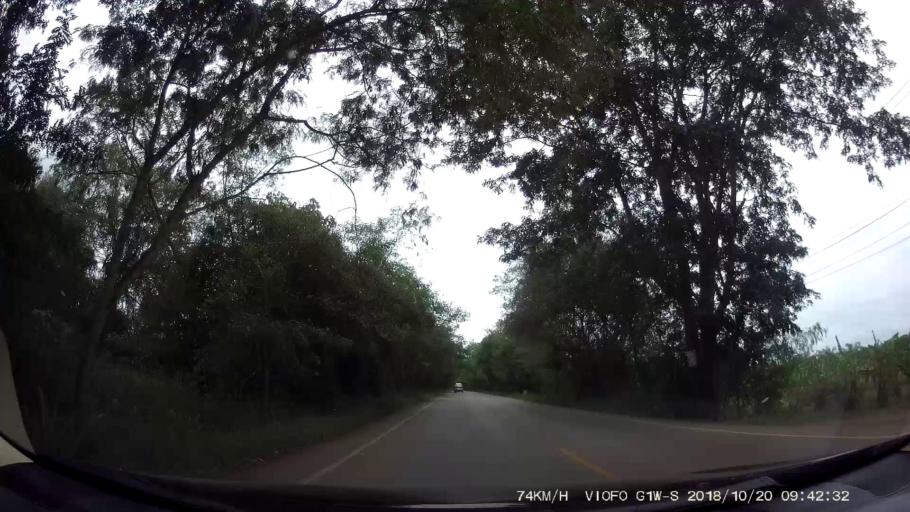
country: TH
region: Chaiyaphum
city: Khon San
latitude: 16.4648
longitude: 101.9520
